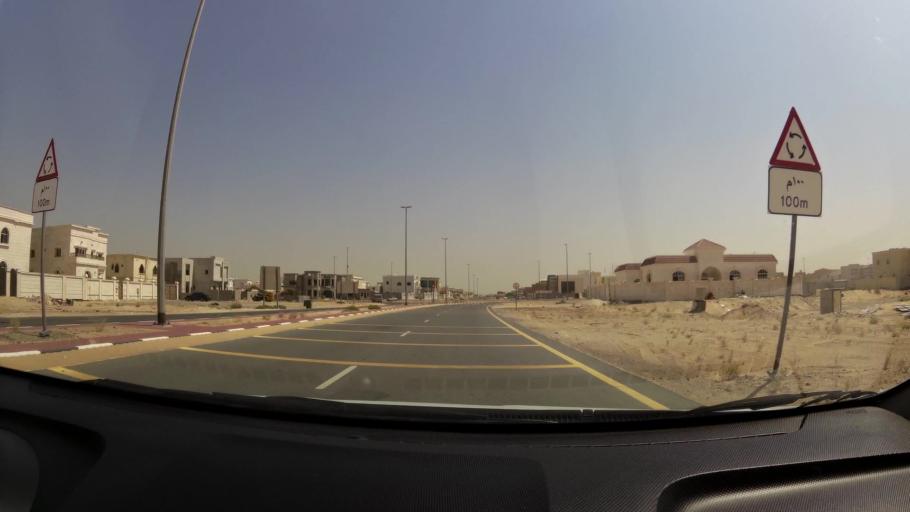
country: AE
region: Ajman
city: Ajman
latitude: 25.4035
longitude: 55.5386
